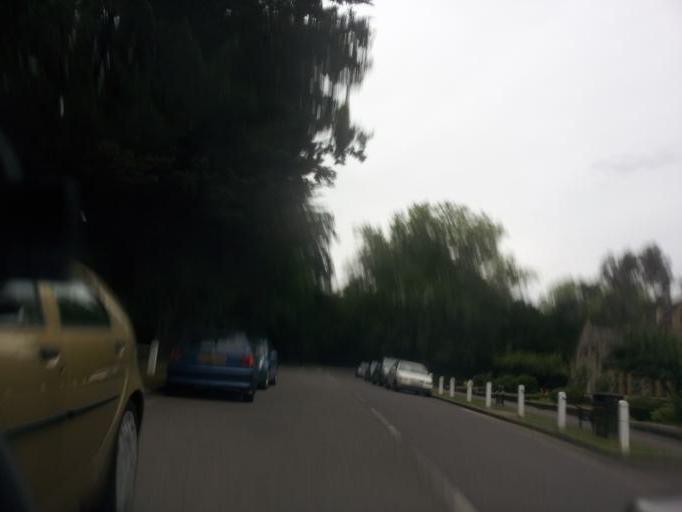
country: GB
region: England
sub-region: Greater London
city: Thornton Heath
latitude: 51.4327
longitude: -0.0784
